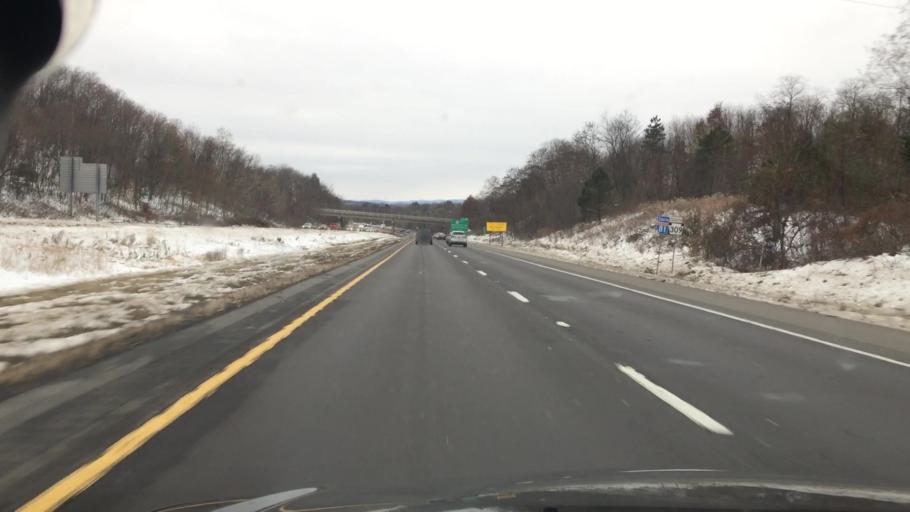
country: US
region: Pennsylvania
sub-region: Luzerne County
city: Georgetown
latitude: 41.2310
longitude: -75.8619
